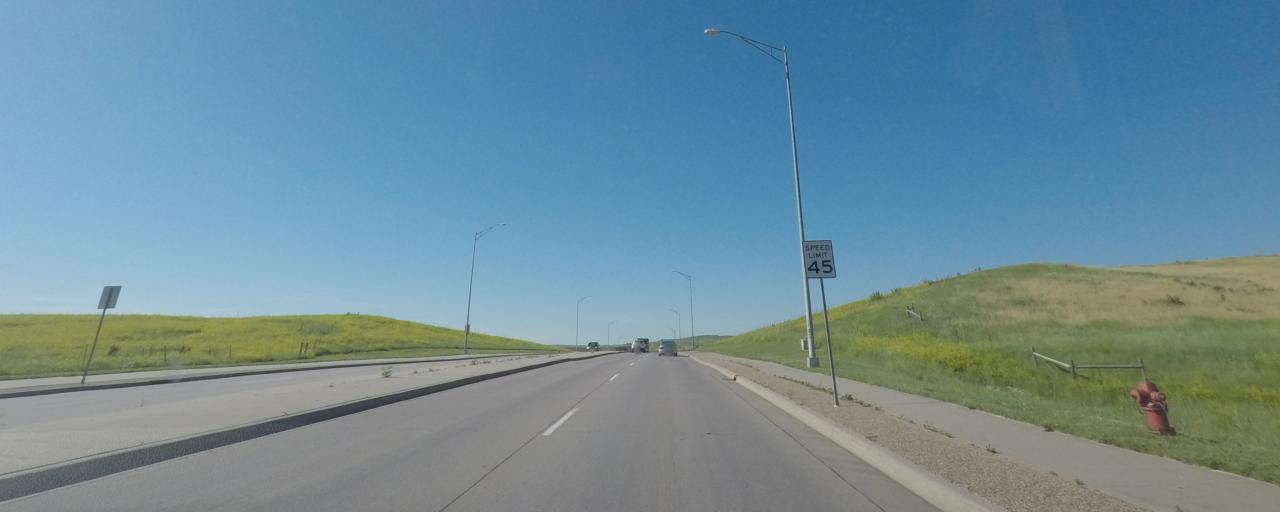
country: US
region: South Dakota
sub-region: Pennington County
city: Rapid City
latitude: 44.0416
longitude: -103.2191
